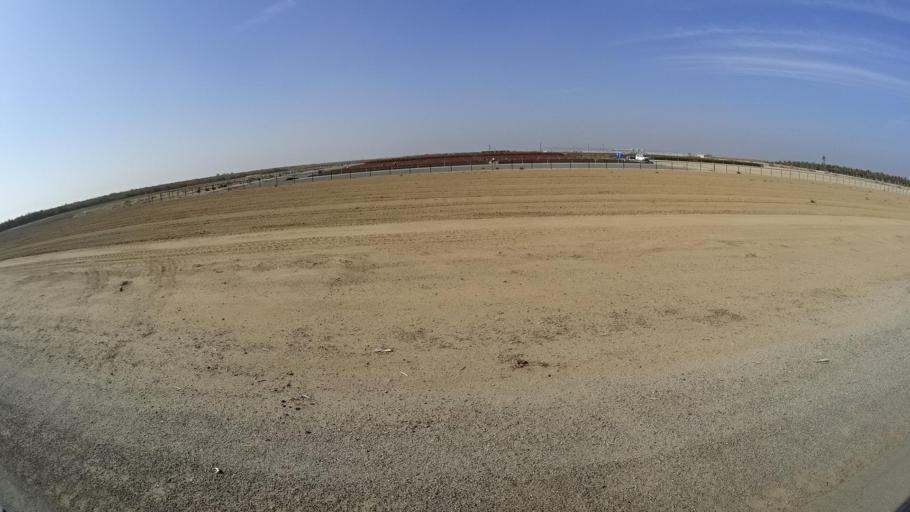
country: US
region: California
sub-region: Kern County
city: McFarland
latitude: 35.6117
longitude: -119.1329
